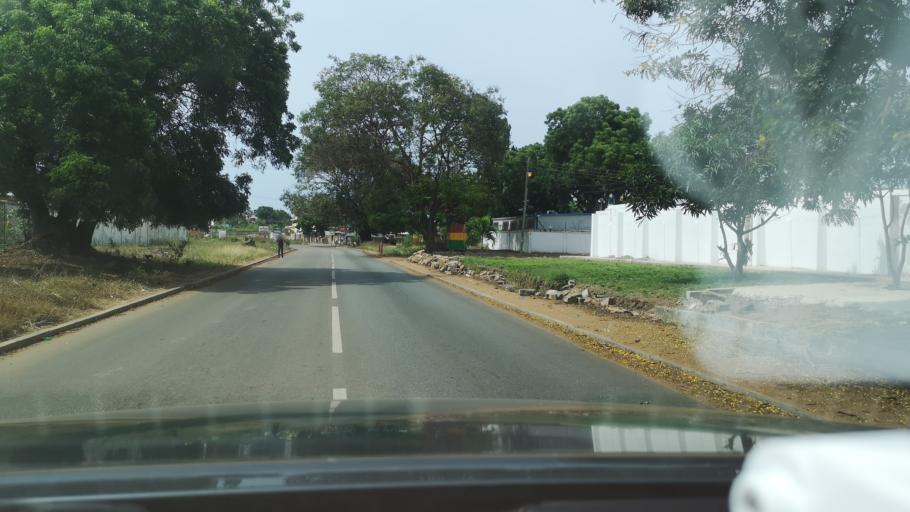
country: GH
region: Greater Accra
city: Tema
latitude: 5.6554
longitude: -0.0222
